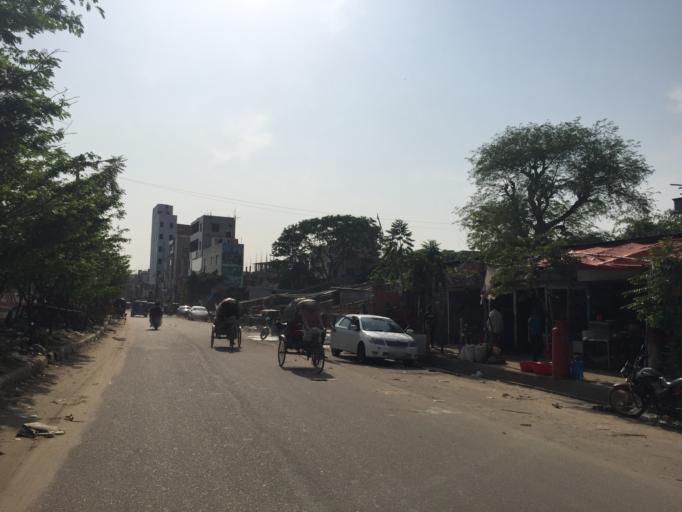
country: BD
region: Dhaka
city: Paltan
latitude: 23.7987
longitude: 90.4330
